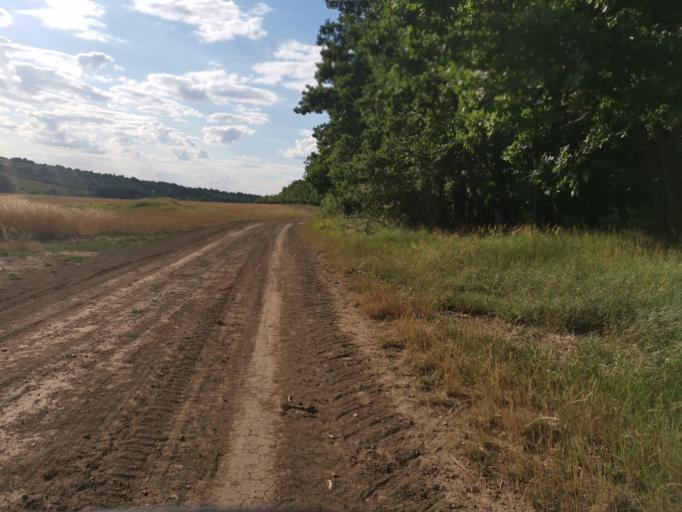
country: SK
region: Trnavsky
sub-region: Okres Skalica
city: Skalica
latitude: 48.8229
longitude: 17.2602
